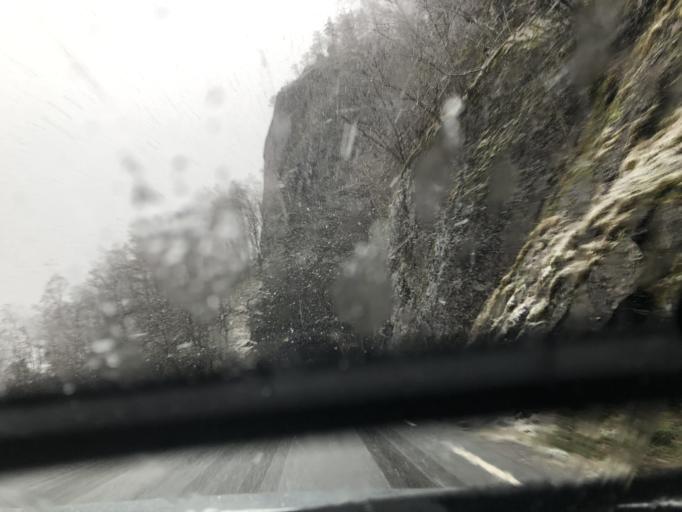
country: NO
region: Rogaland
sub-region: Suldal
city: Sand
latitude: 59.4157
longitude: 6.2184
